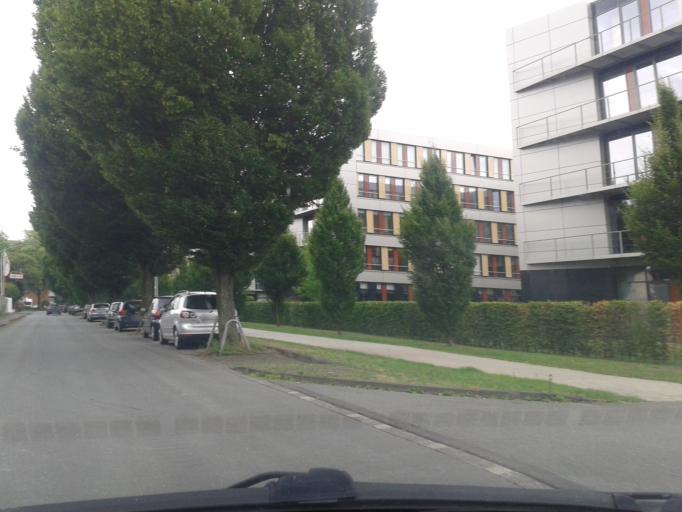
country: DE
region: North Rhine-Westphalia
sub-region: Regierungsbezirk Detmold
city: Paderborn
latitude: 51.7219
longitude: 8.7352
